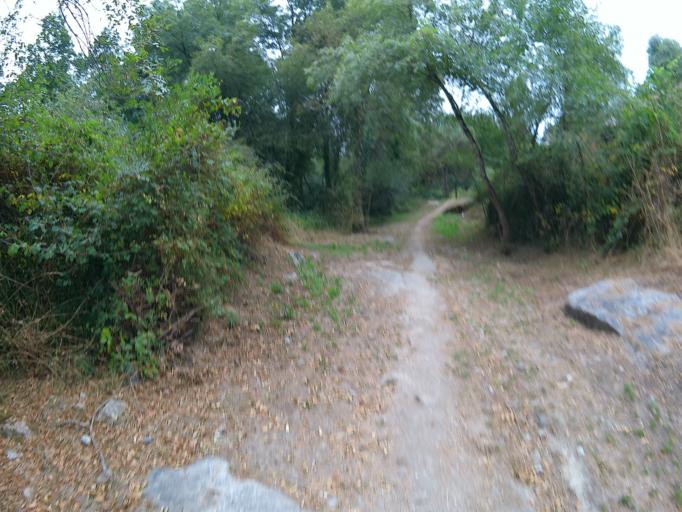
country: PT
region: Viana do Castelo
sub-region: Ponte da Barca
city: Ponte da Barca
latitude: 41.8007
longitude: -8.4741
